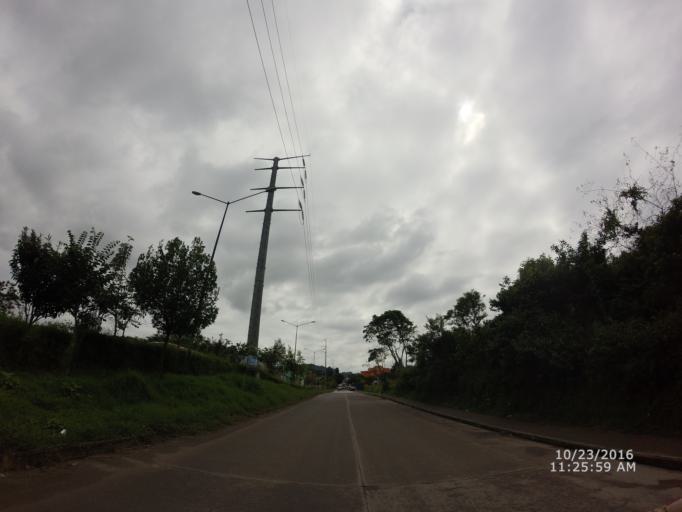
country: MX
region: Veracruz
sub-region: Tlalnelhuayocan
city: Guadalupe Victoria
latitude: 19.5507
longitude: -96.9433
